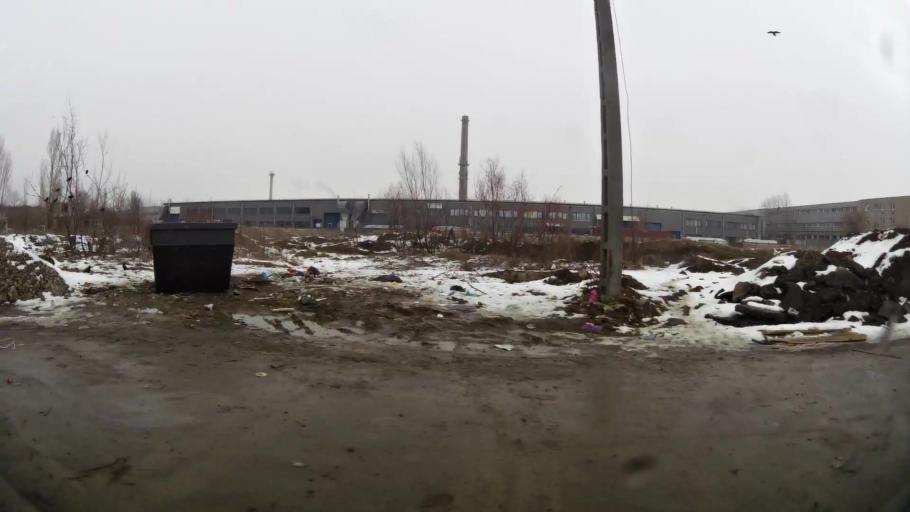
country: RO
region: Ilfov
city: Dobroesti
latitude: 44.4215
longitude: 26.1874
